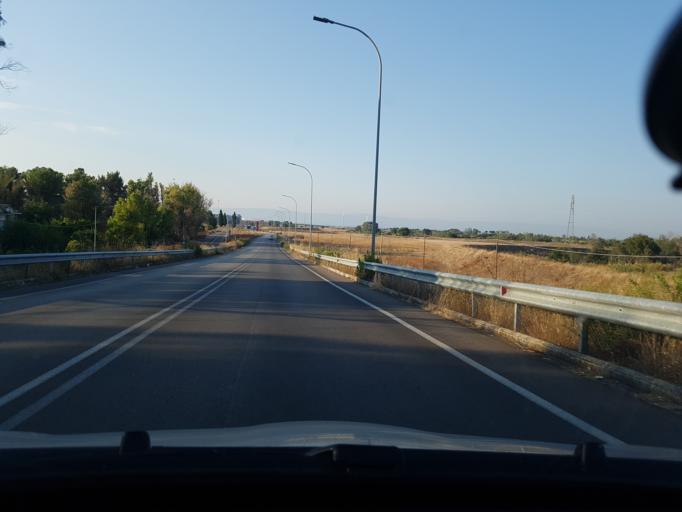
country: IT
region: Apulia
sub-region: Provincia di Foggia
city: Carapelle
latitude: 41.4082
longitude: 15.6531
